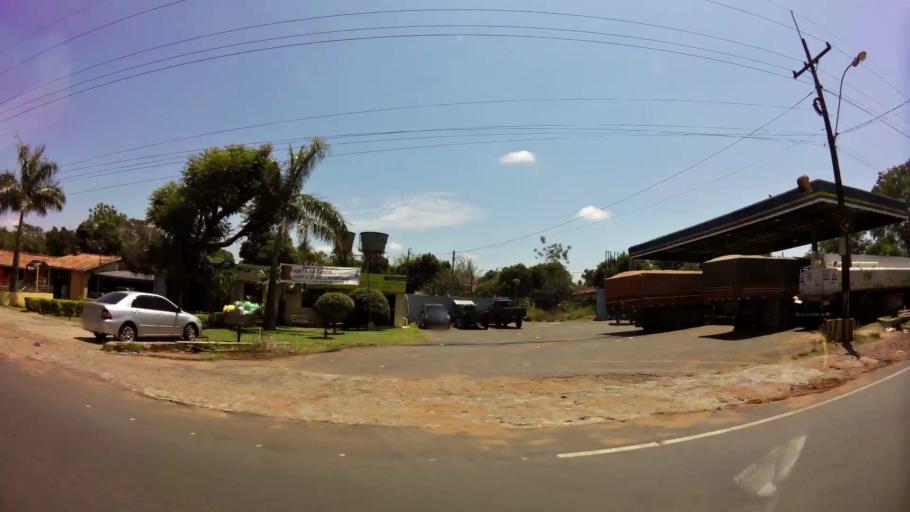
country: PY
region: Central
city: San Antonio
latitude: -25.4124
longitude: -57.5511
